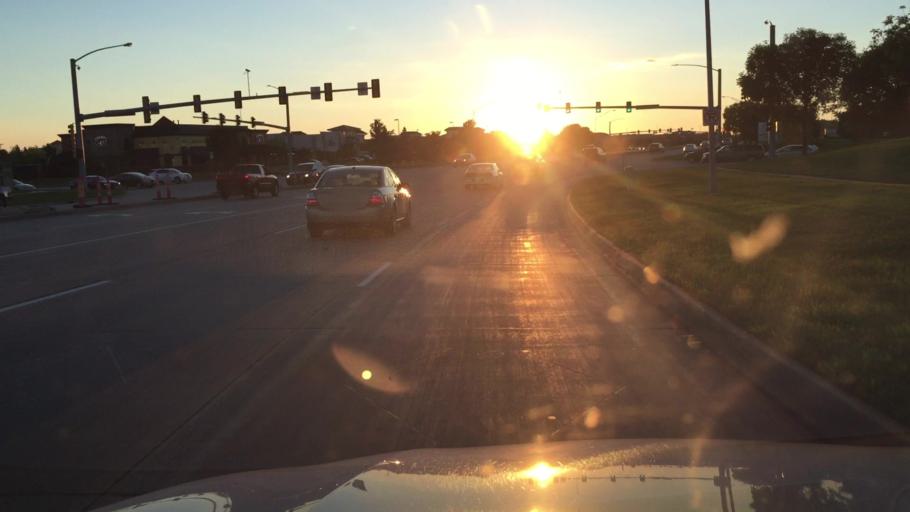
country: US
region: Iowa
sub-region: Polk County
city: Clive
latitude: 41.5594
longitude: -93.7933
